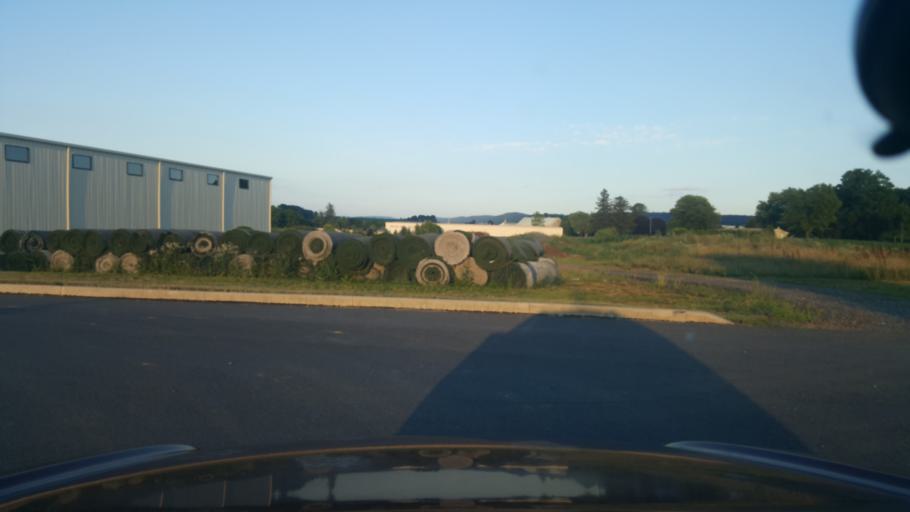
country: US
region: Pennsylvania
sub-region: Lebanon County
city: Campbelltown
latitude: 40.2860
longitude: -76.5678
